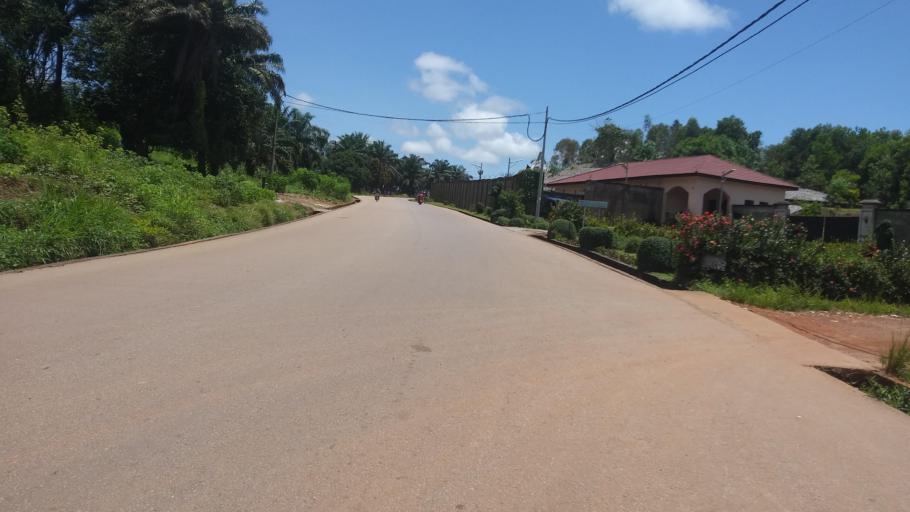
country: SL
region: Northern Province
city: Makeni
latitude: 8.8792
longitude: -12.0276
